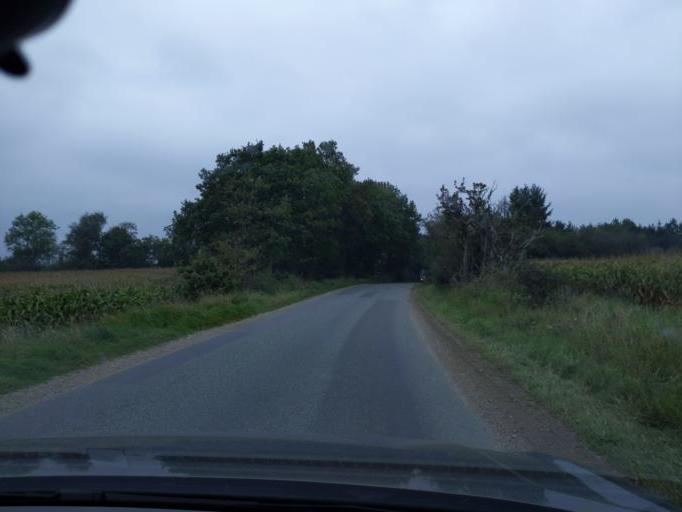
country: DK
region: Central Jutland
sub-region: Viborg Kommune
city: Stoholm
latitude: 56.5132
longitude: 9.2544
